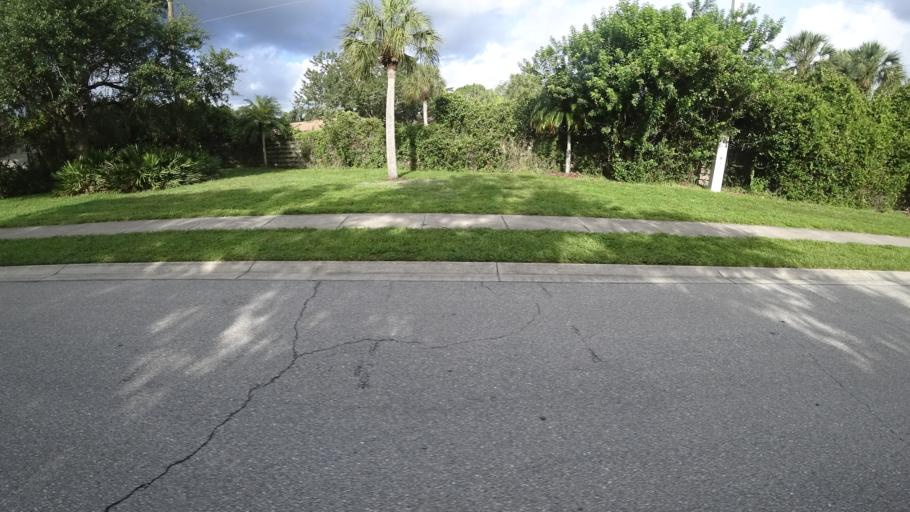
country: US
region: Florida
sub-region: Sarasota County
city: Desoto Lakes
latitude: 27.4139
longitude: -82.4848
